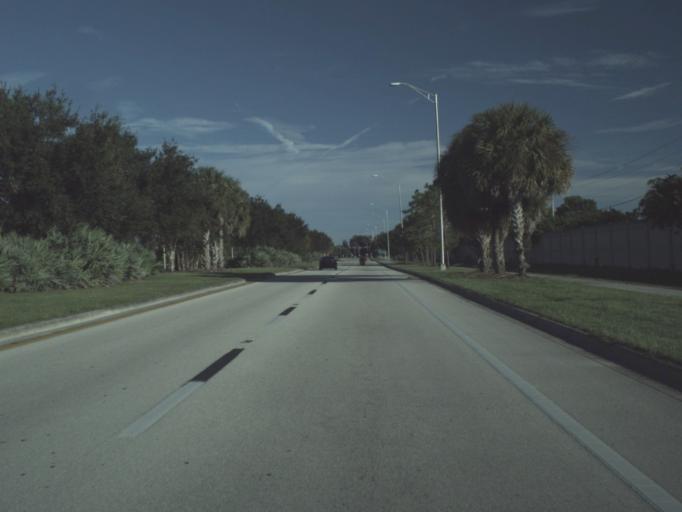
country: US
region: Florida
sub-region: Lee County
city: Palmona Park
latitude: 26.6923
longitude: -81.8878
